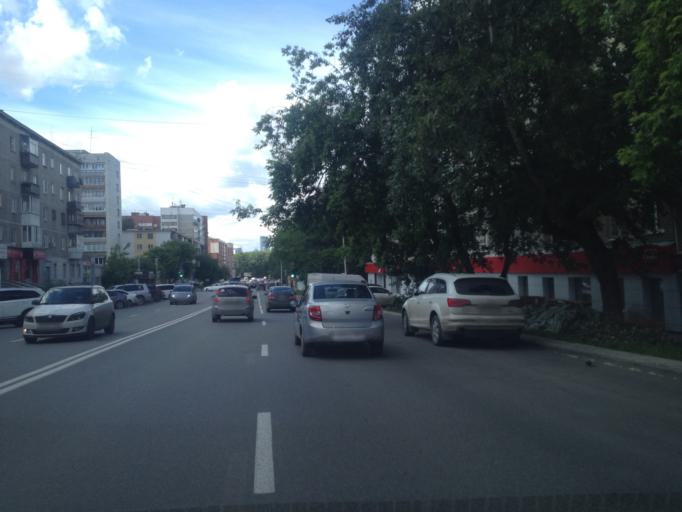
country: RU
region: Sverdlovsk
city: Yekaterinburg
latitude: 56.8116
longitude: 60.6003
